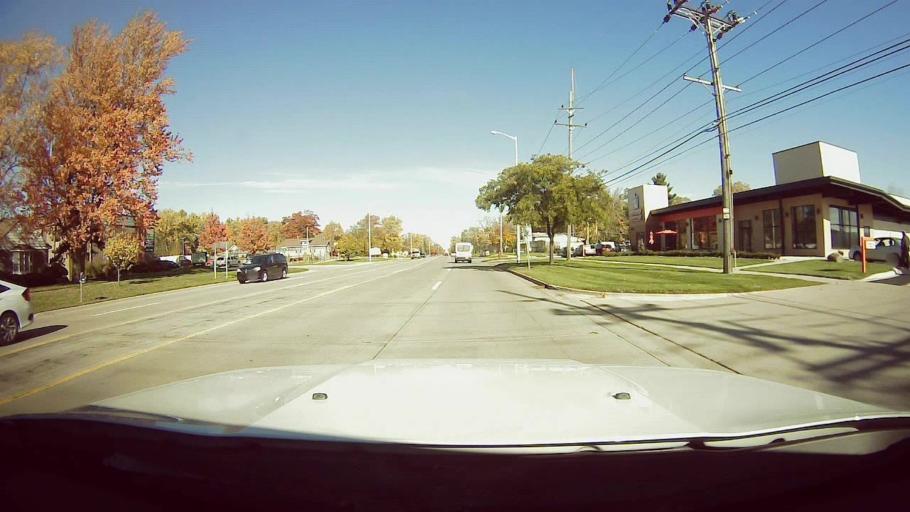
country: US
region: Michigan
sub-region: Oakland County
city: Farmington
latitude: 42.4415
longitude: -83.3753
